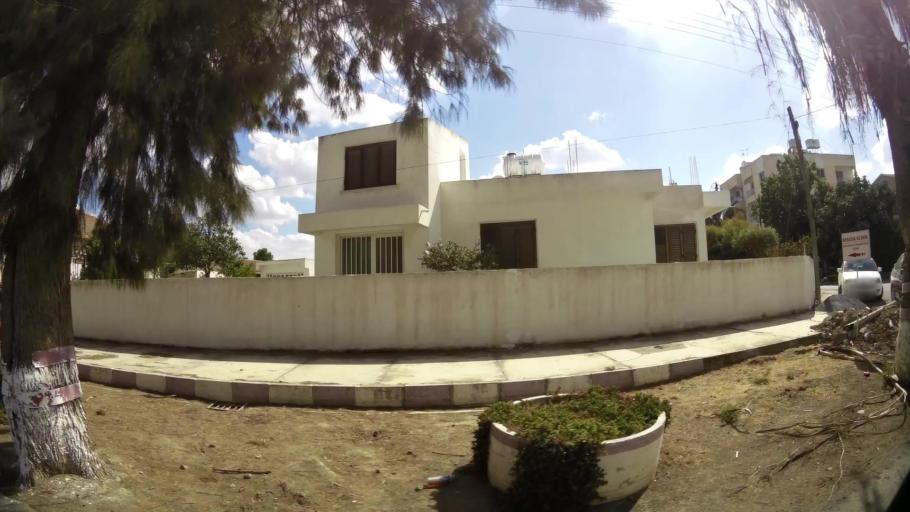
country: CY
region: Lefkosia
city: Nicosia
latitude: 35.1851
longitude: 33.3708
